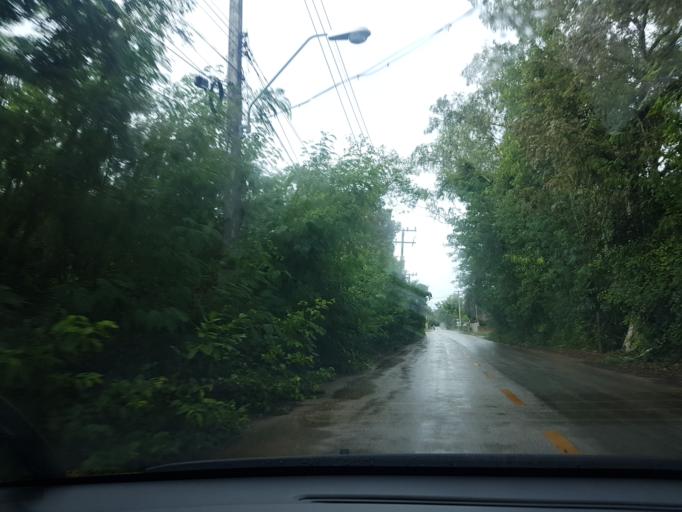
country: TH
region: Lampang
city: Lampang
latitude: 18.2987
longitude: 99.4736
